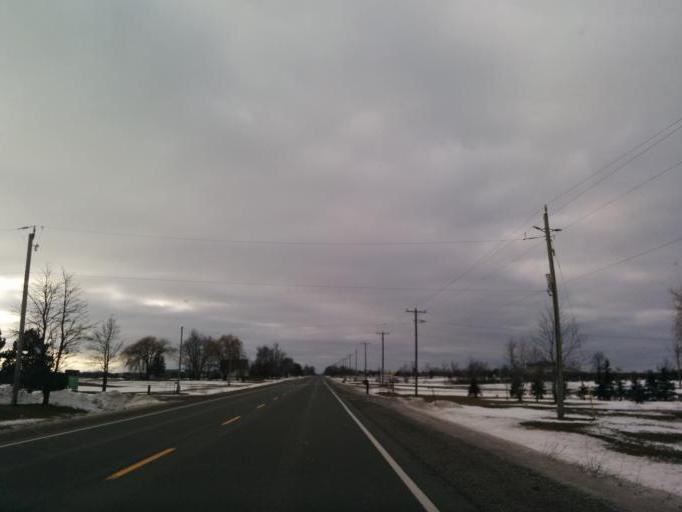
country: CA
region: Ontario
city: Ancaster
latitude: 42.9421
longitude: -79.8901
